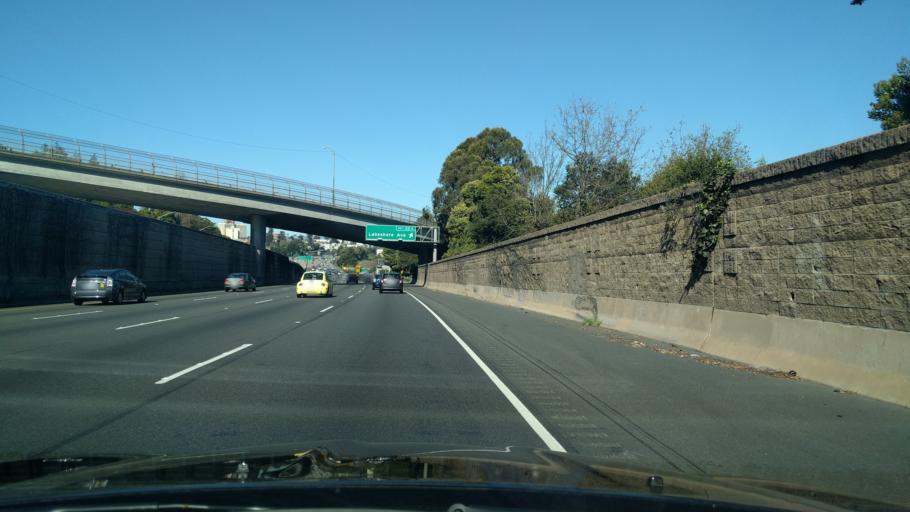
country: US
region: California
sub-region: Alameda County
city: Piedmont
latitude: 37.8082
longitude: -122.2408
